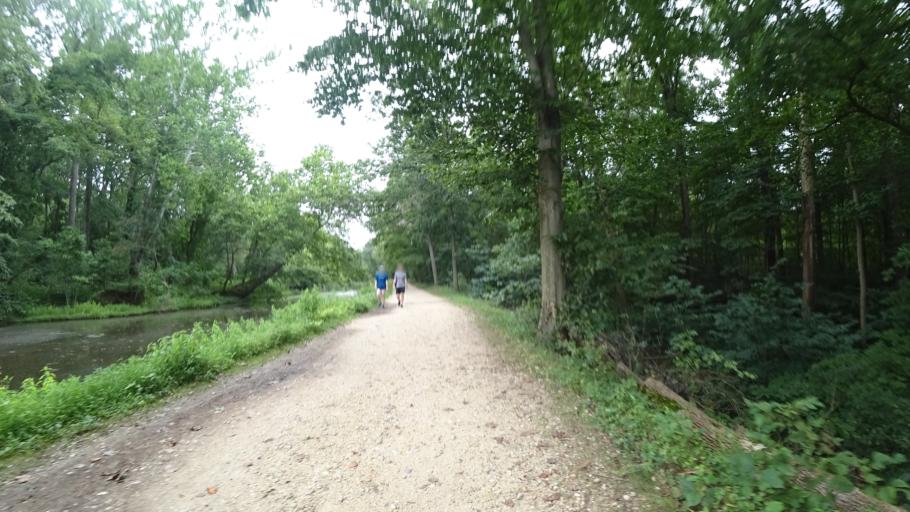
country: US
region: Maryland
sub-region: Montgomery County
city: Potomac
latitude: 38.9774
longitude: -77.2223
